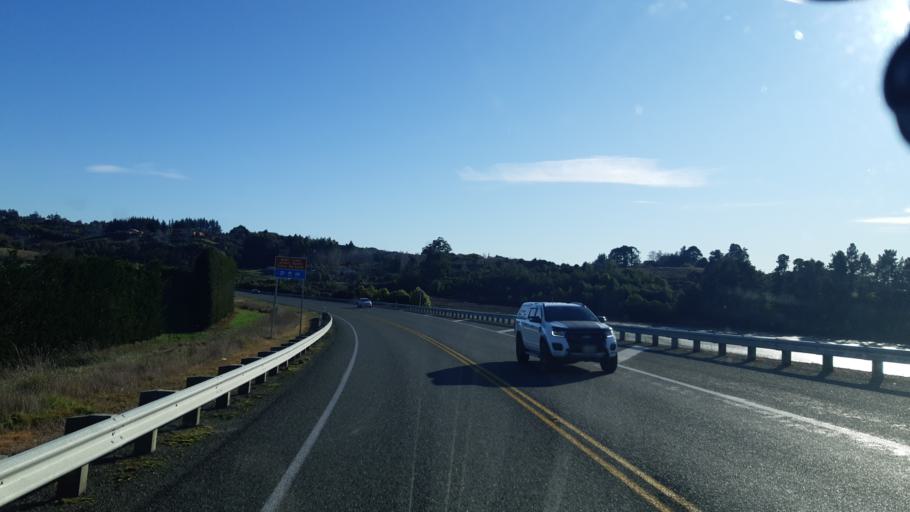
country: NZ
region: Tasman
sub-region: Tasman District
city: Mapua
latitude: -41.2568
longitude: 173.0730
